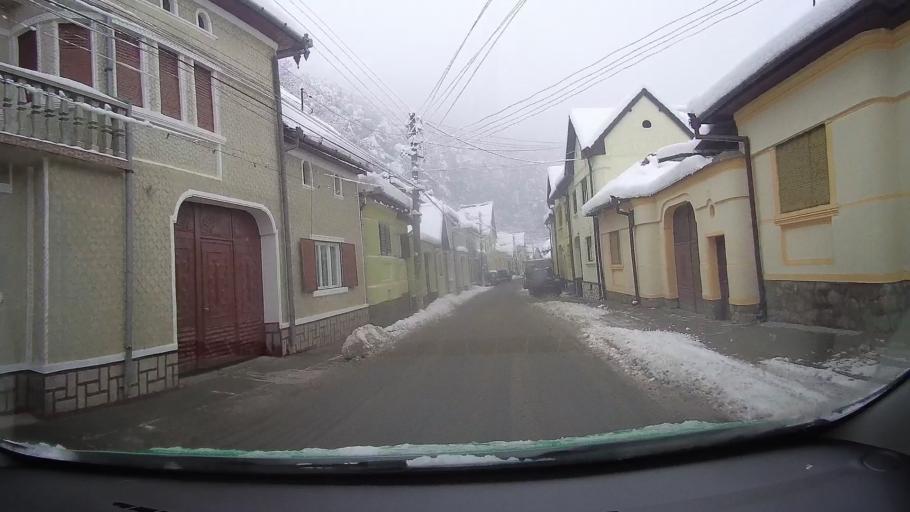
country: RO
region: Sibiu
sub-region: Comuna Tilisca
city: Tilisca
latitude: 45.8012
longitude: 23.8417
